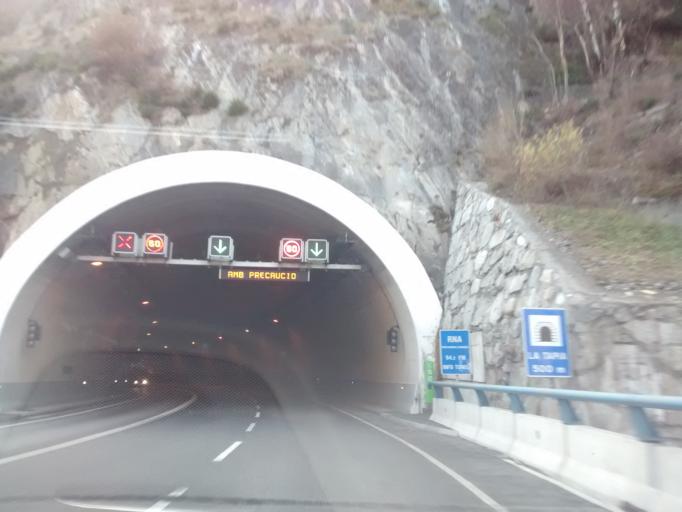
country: AD
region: Sant Julia de Loria
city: Sant Julia de Loria
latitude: 42.4742
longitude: 1.4905
